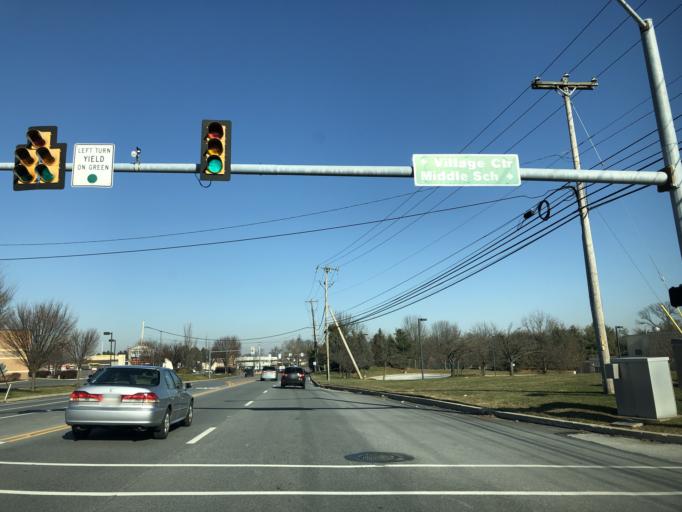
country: US
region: Pennsylvania
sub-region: Chester County
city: Exton
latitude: 40.0478
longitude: -75.6622
